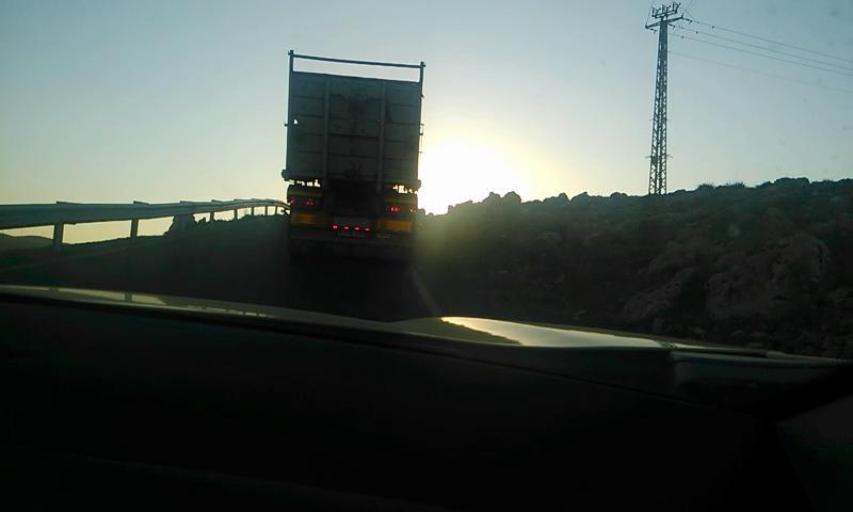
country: PS
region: West Bank
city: Rammun
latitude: 31.9144
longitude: 35.3502
